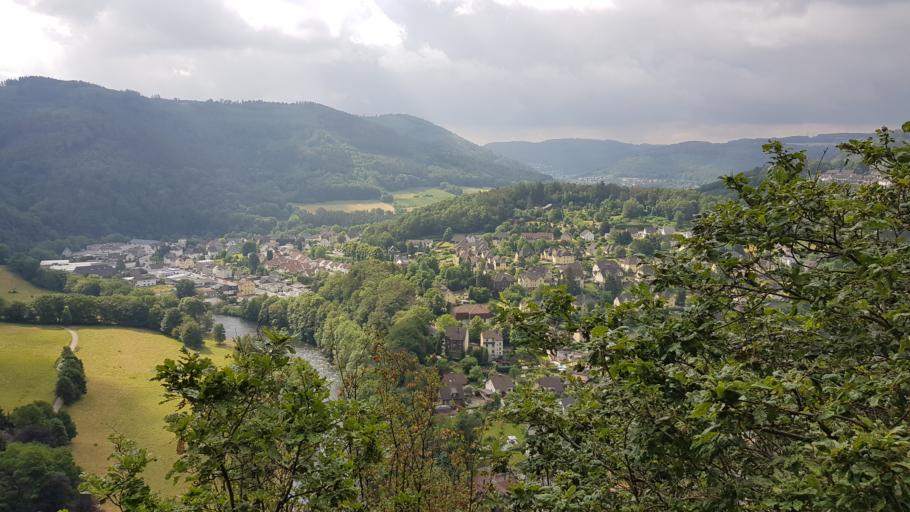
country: DE
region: North Rhine-Westphalia
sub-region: Regierungsbezirk Arnsberg
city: Nachrodt-Wiblingwerde
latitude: 51.3392
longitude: 7.6420
